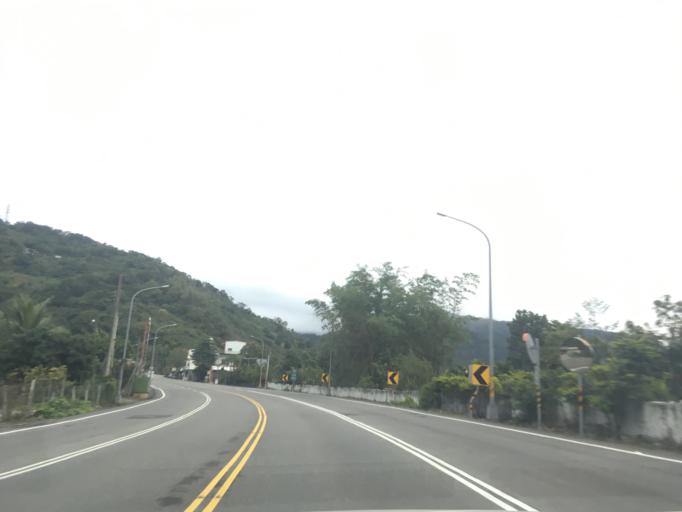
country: TW
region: Taiwan
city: Taitung City
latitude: 22.7473
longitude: 121.0567
